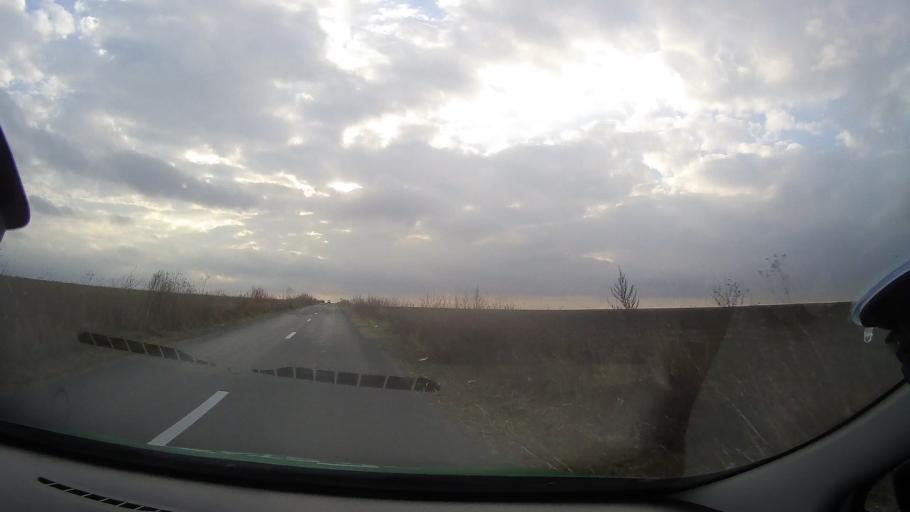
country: RO
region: Constanta
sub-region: Comuna Deleni
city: Pietreni
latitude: 44.1279
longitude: 28.1110
